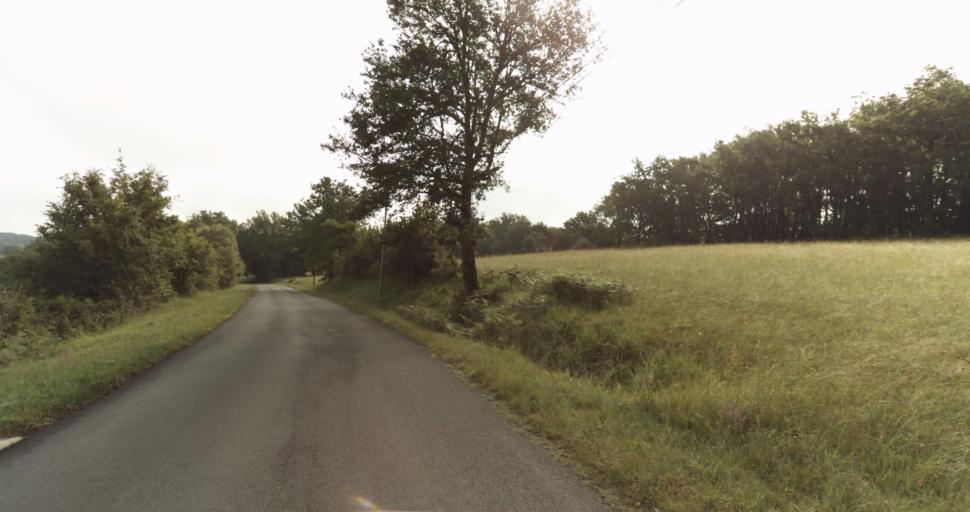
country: FR
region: Aquitaine
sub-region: Departement de la Dordogne
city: Lalinde
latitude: 44.9110
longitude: 0.7919
